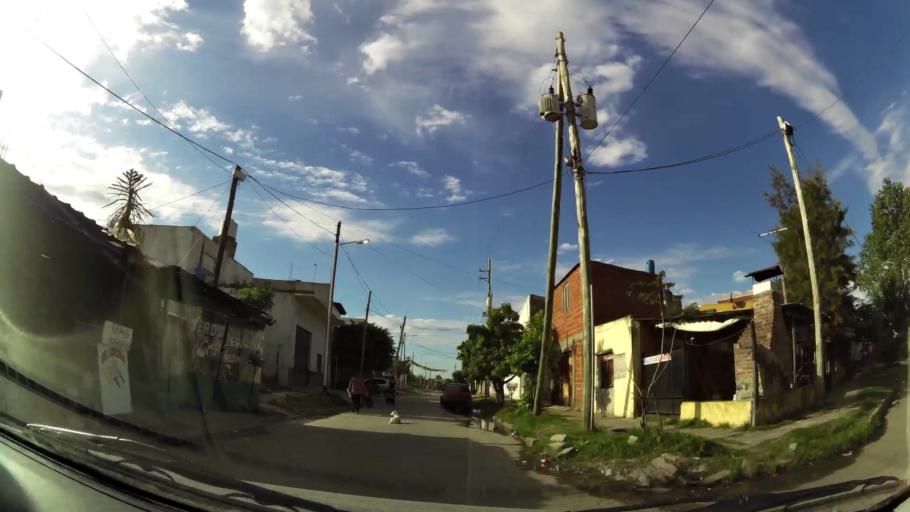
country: AR
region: Buenos Aires
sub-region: Partido de Lanus
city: Lanus
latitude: -34.7028
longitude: -58.3581
